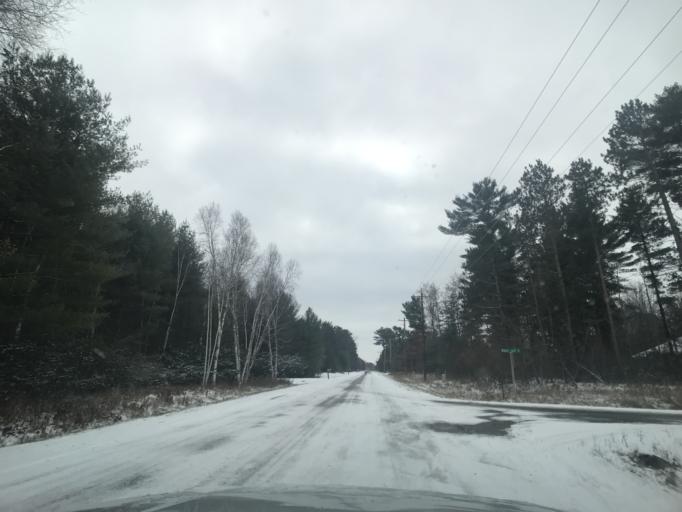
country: US
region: Wisconsin
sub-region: Brown County
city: Suamico
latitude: 44.7001
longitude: -88.1009
